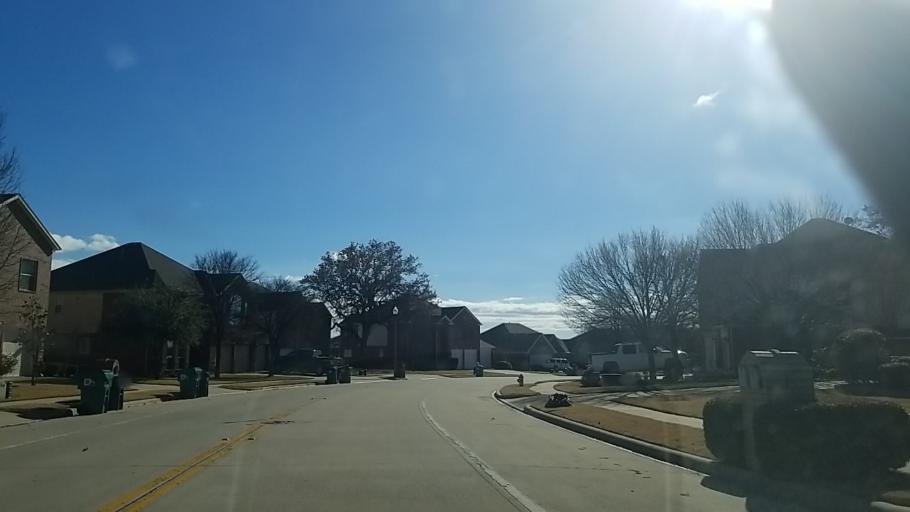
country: US
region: Texas
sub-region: Denton County
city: Corinth
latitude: 33.1528
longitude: -97.0910
